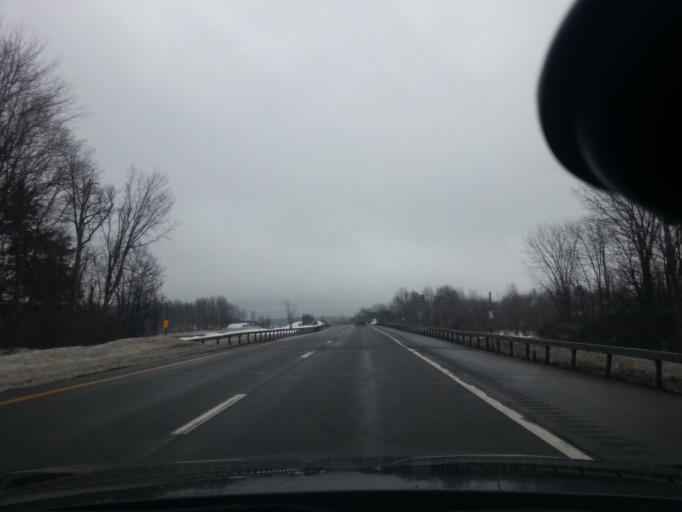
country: US
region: New York
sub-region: Oswego County
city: Pulaski
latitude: 43.5253
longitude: -76.1209
